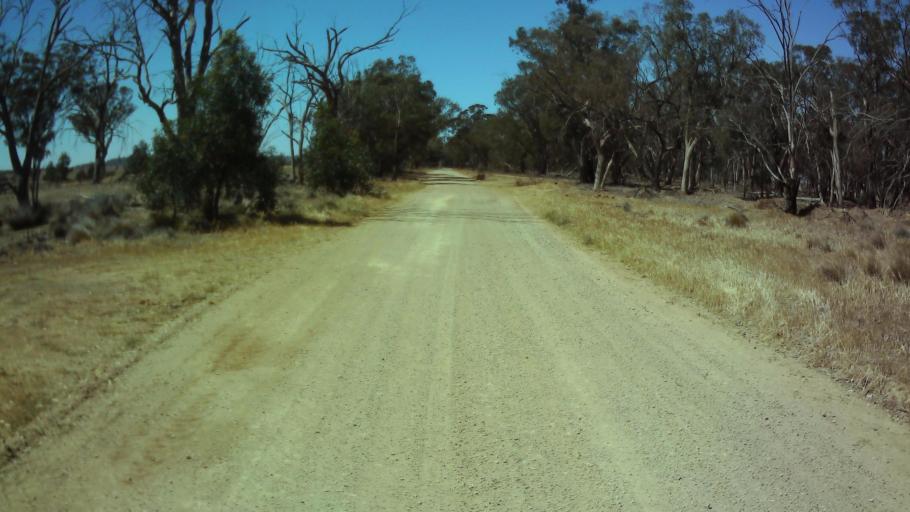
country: AU
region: New South Wales
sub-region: Weddin
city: Grenfell
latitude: -33.8732
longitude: 148.0887
